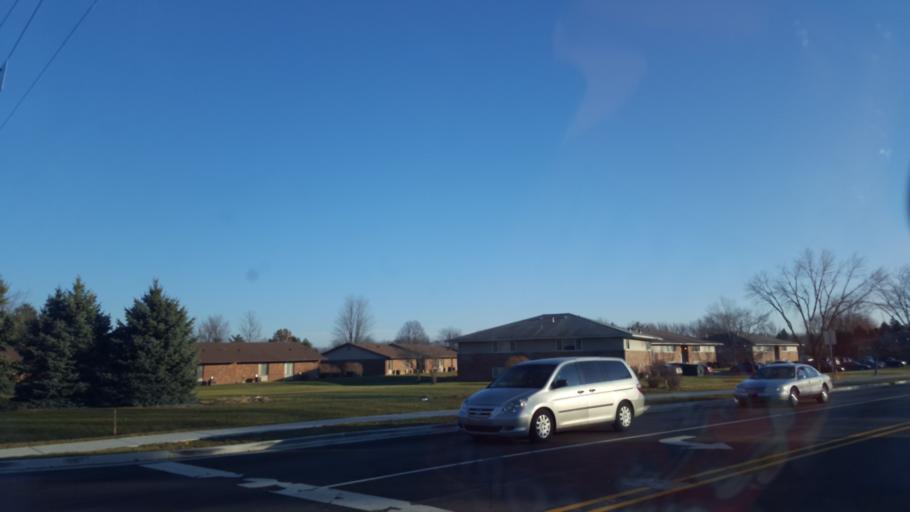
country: US
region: Indiana
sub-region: Elkhart County
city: Nappanee
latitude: 41.4570
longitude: -86.0015
